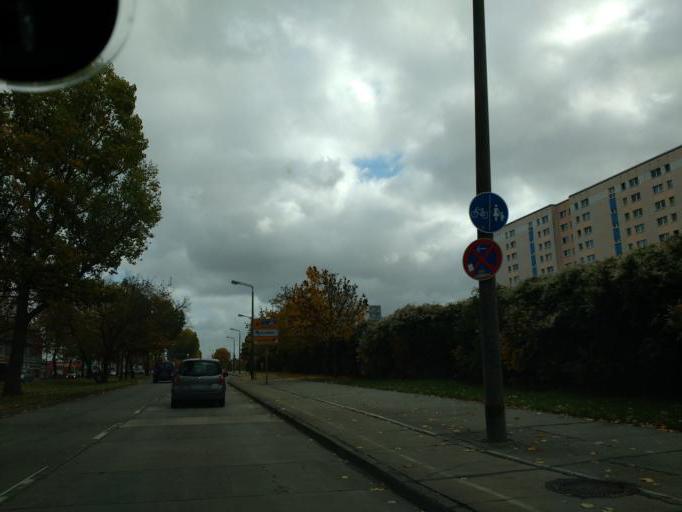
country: DE
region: Berlin
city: Marzahn
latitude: 52.5489
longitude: 13.5905
